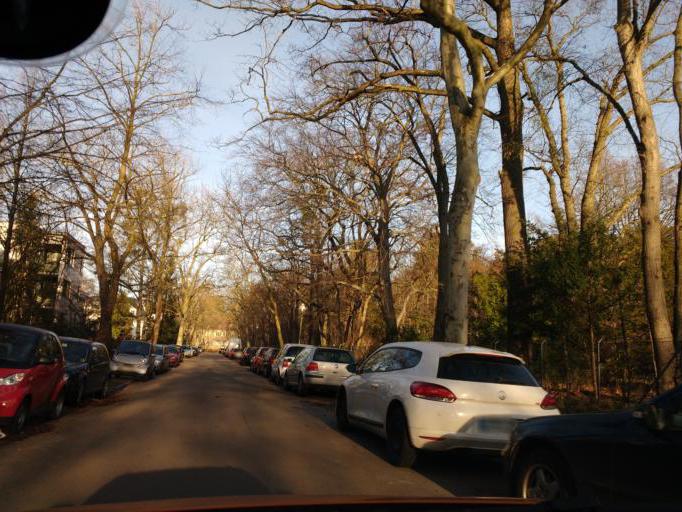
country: DE
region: Berlin
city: Nikolassee
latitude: 52.4307
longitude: 13.2174
